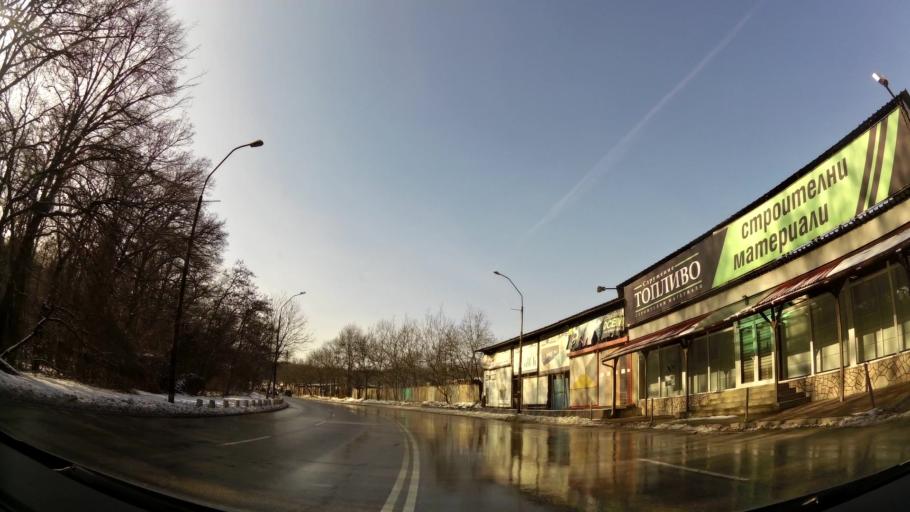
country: BG
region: Sofia-Capital
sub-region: Stolichna Obshtina
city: Sofia
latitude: 42.6667
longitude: 23.3416
